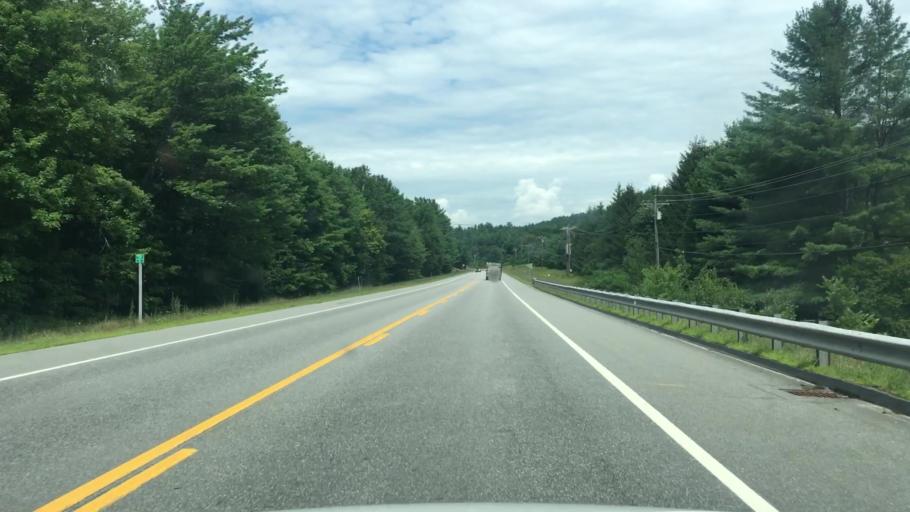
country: US
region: New Hampshire
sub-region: Grafton County
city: Rumney
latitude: 43.8498
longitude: -71.9114
